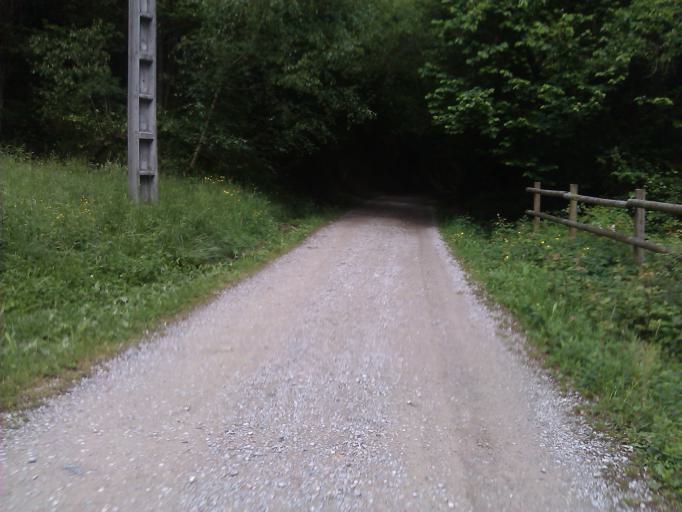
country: ES
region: Navarre
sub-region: Provincia de Navarra
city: Leitza
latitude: 43.0912
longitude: -1.9288
